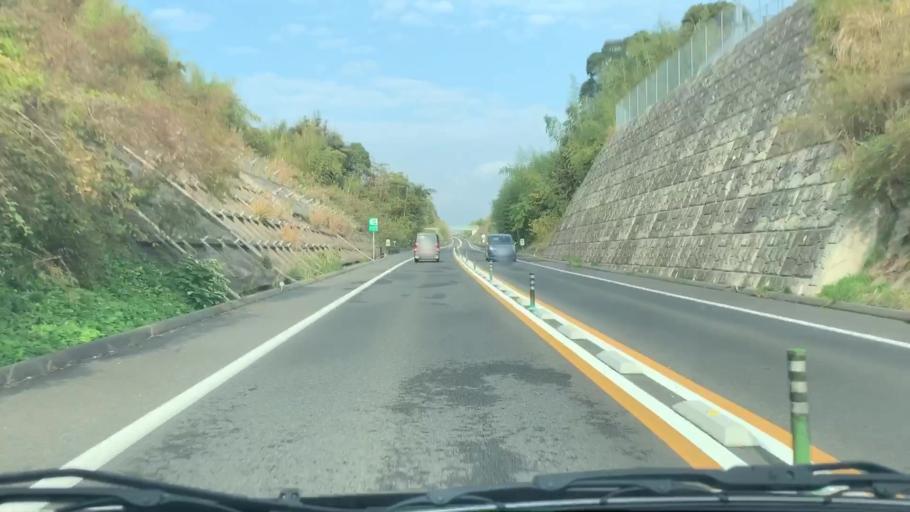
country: JP
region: Nagasaki
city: Sasebo
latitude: 33.0211
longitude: 129.7334
